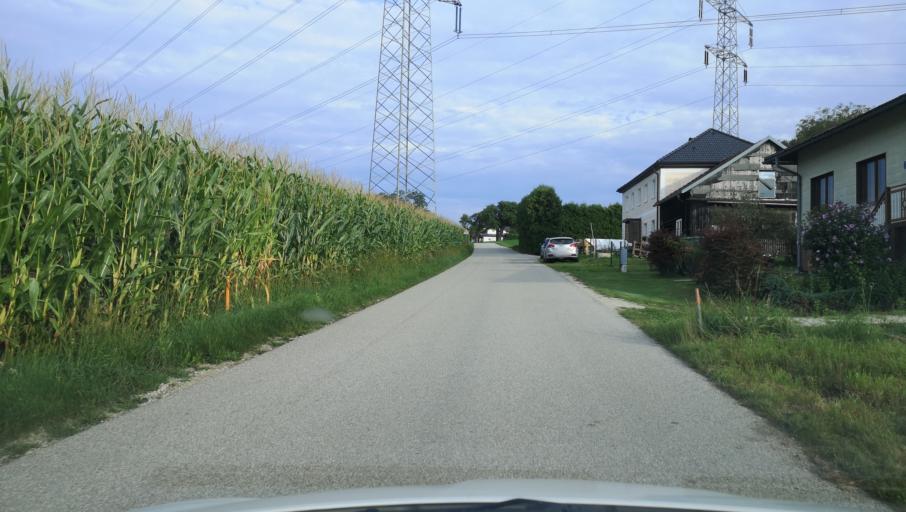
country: AT
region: Lower Austria
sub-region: Politischer Bezirk Amstetten
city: Amstetten
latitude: 48.1535
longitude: 14.8824
